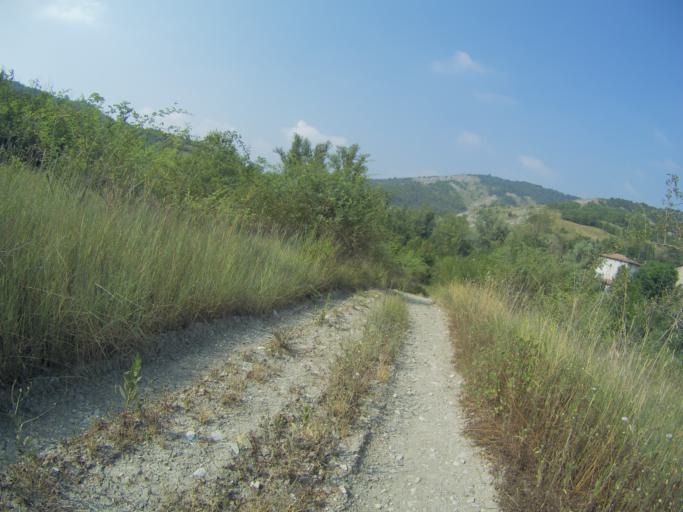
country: IT
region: Emilia-Romagna
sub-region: Provincia di Reggio Emilia
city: Ventoso
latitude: 44.5756
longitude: 10.6570
